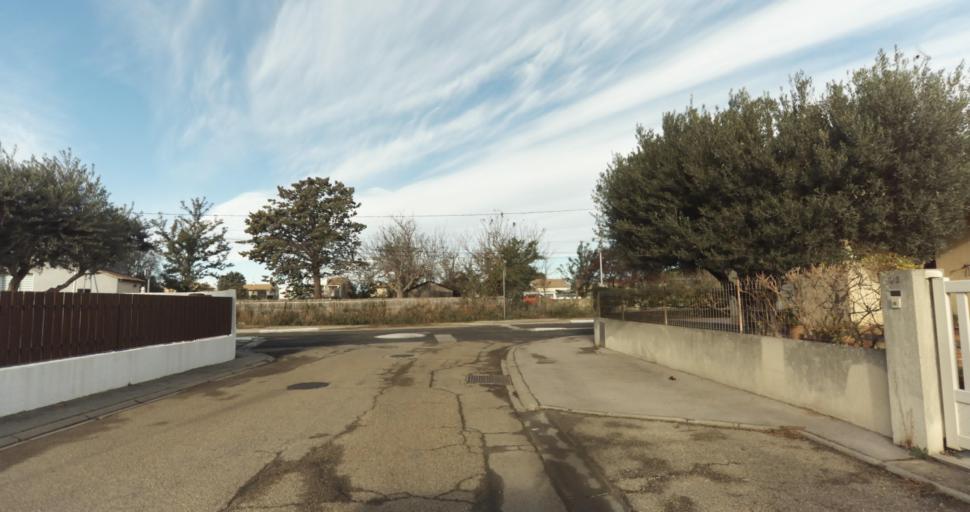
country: FR
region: Languedoc-Roussillon
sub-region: Departement du Gard
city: Aigues-Mortes
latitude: 43.5736
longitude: 4.1982
